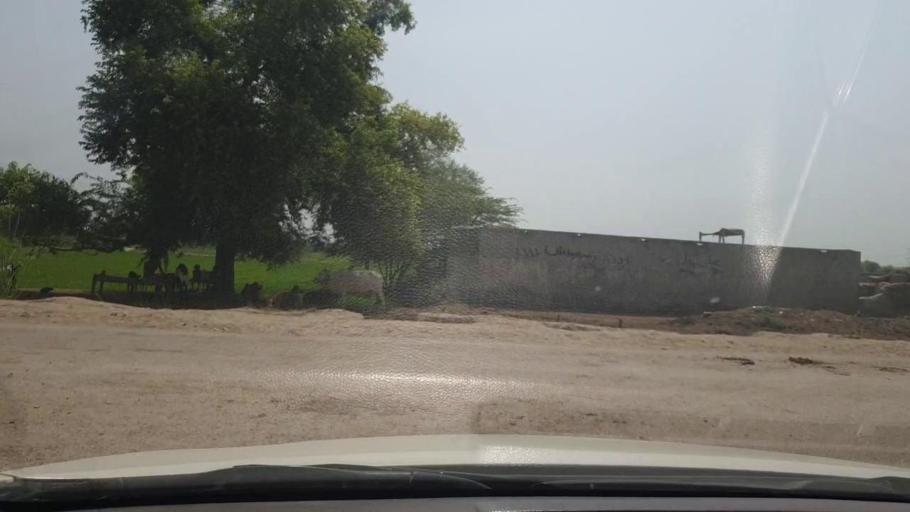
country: PK
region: Sindh
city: Shikarpur
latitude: 28.0181
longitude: 68.6622
